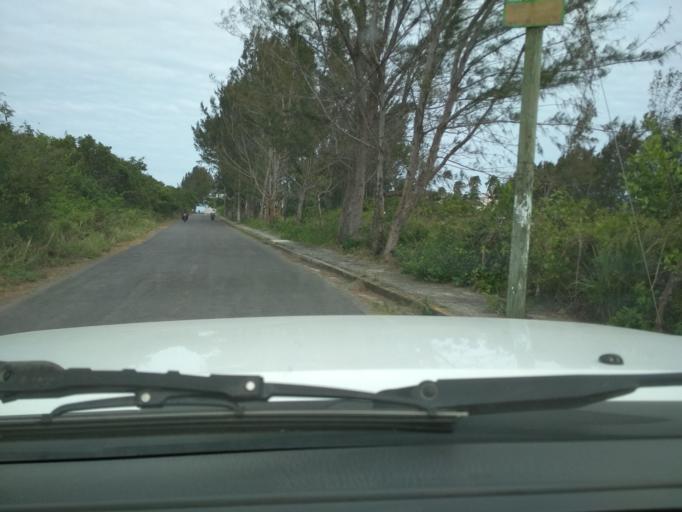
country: MX
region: Veracruz
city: Anton Lizardo
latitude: 19.0395
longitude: -95.9725
